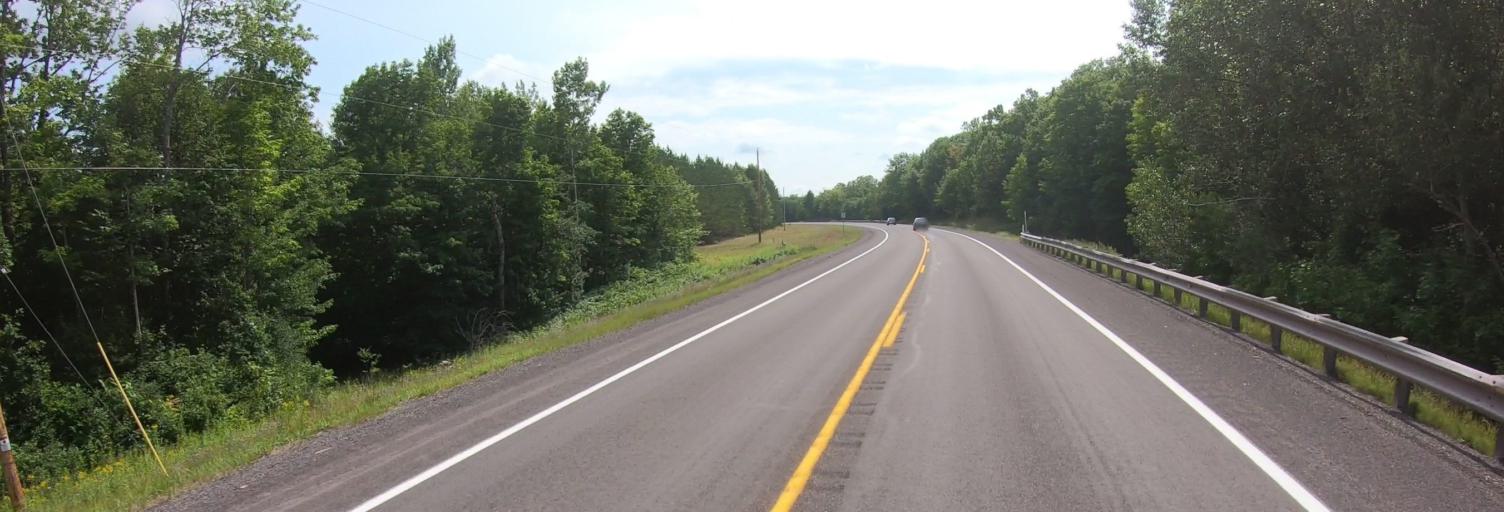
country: US
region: Michigan
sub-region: Houghton County
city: Hancock
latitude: 46.9927
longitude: -88.7782
